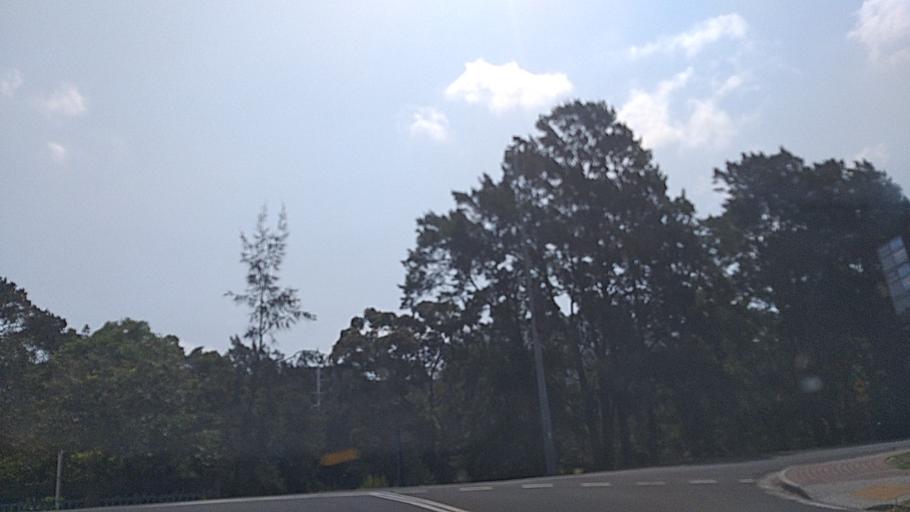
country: AU
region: New South Wales
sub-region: Wollongong
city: Mount Ousley
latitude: -34.4069
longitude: 150.8768
